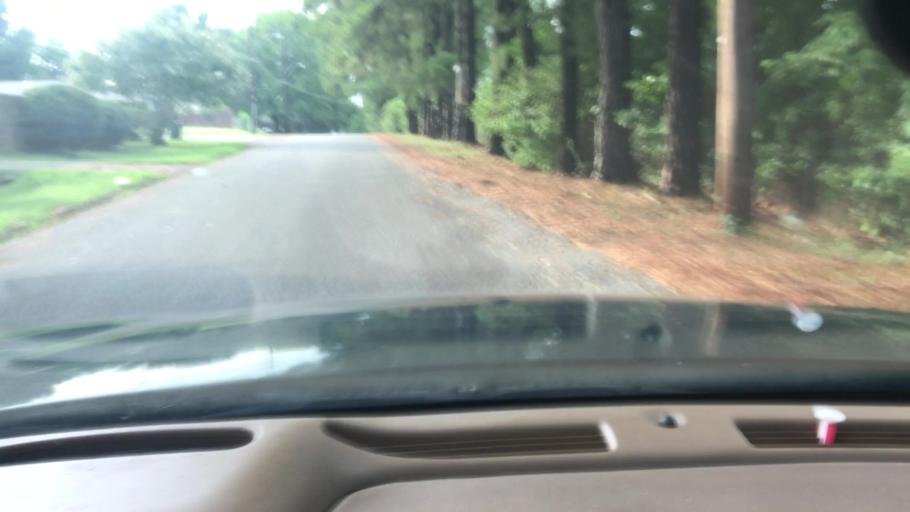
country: US
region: Mississippi
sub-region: De Soto County
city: Southaven
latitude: 35.0463
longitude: -90.0087
